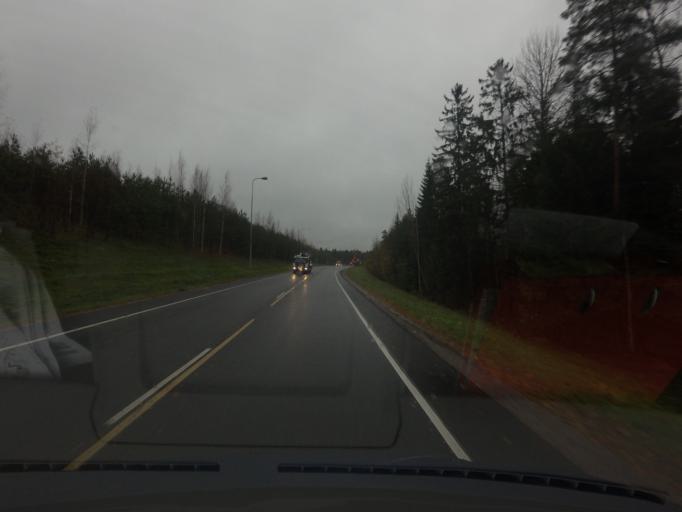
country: FI
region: Uusimaa
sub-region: Helsinki
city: Kauniainen
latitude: 60.2225
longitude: 24.7498
